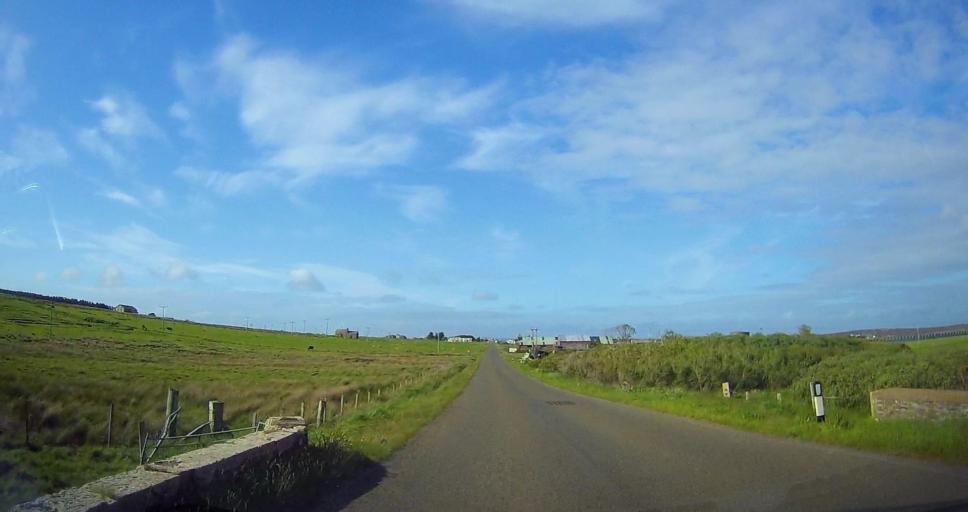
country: GB
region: Scotland
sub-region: Orkney Islands
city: Stromness
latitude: 58.8255
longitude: -3.2096
